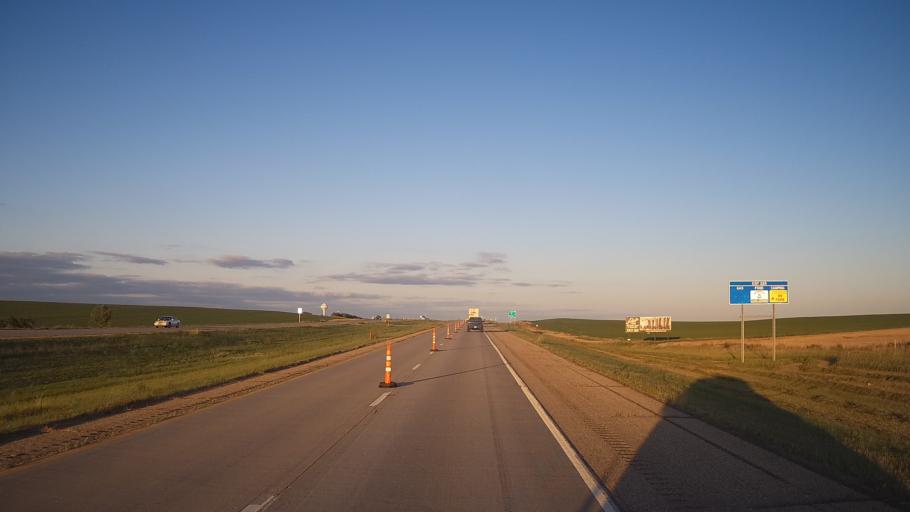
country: US
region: South Dakota
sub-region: Lyman County
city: Kennebec
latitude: 43.8984
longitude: -100.0783
